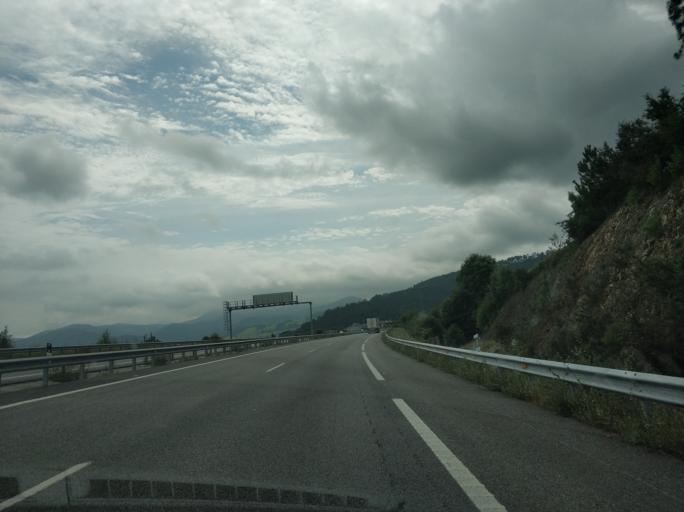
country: ES
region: Asturias
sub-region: Province of Asturias
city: Navia
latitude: 43.5338
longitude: -6.5873
